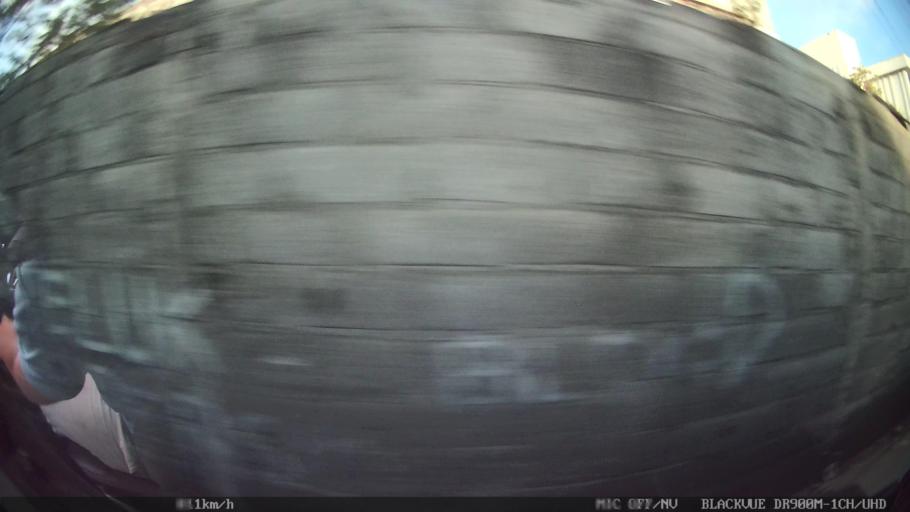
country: ID
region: Bali
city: Bualu
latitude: -8.7593
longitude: 115.2195
